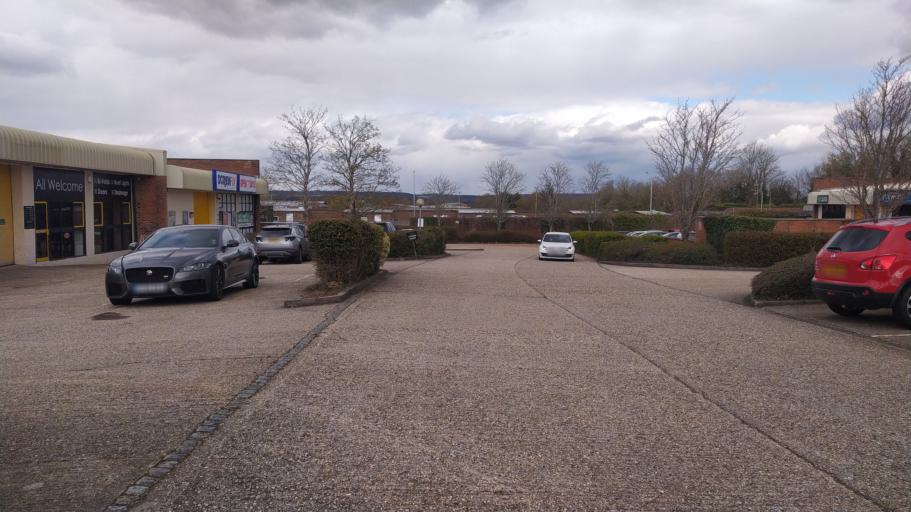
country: GB
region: England
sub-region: Hampshire
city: Andover
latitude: 51.2114
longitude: -1.5102
